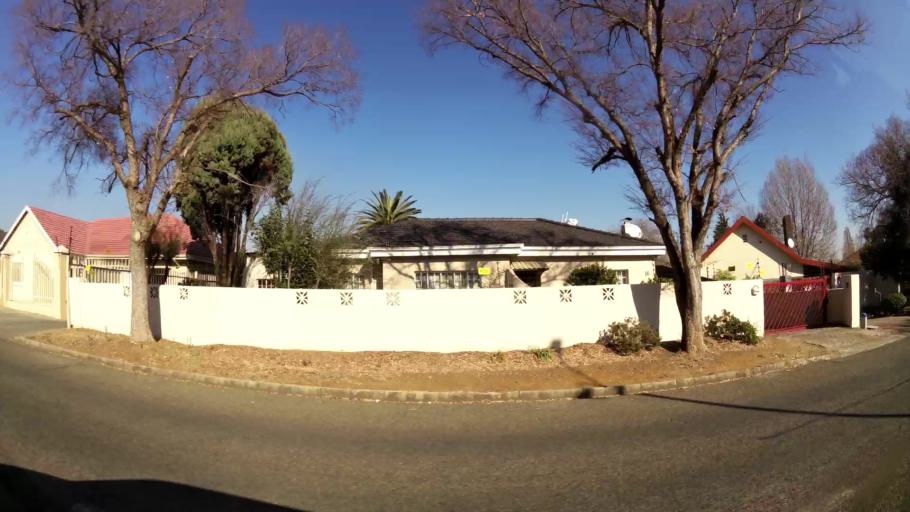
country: ZA
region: Gauteng
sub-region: City of Johannesburg Metropolitan Municipality
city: Modderfontein
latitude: -26.1589
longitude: 28.1556
